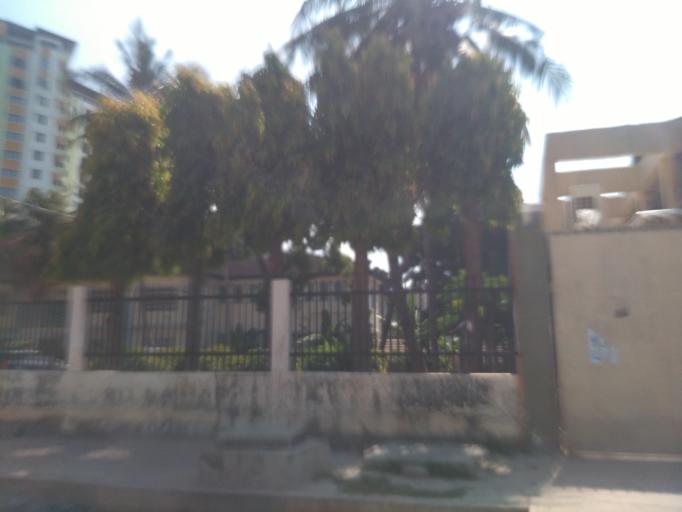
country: TZ
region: Dar es Salaam
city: Dar es Salaam
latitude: -6.8055
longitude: 39.2812
